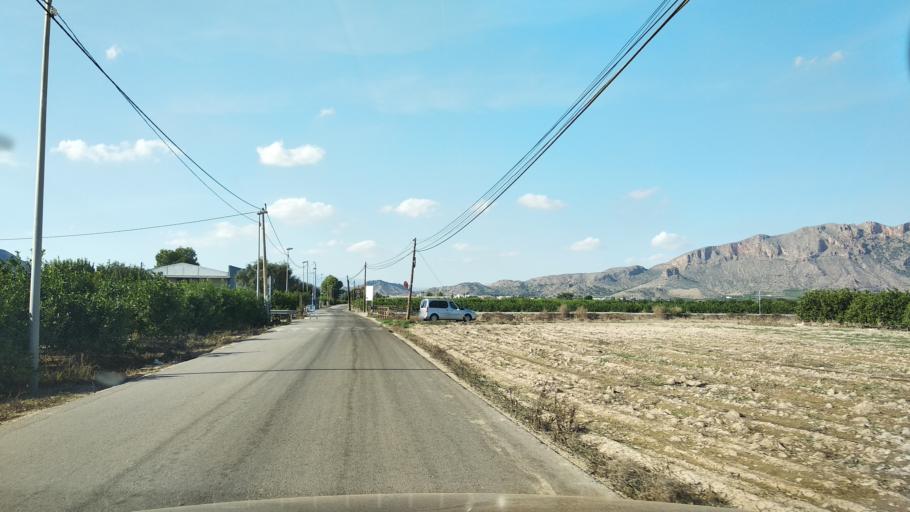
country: ES
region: Murcia
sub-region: Murcia
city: Santomera
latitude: 38.0469
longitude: -1.0381
